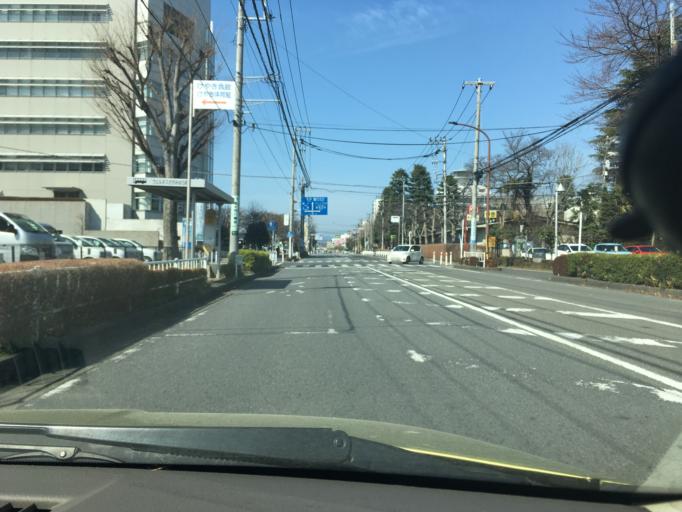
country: JP
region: Tokyo
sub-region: Machida-shi
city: Machida
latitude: 35.5697
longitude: 139.3751
